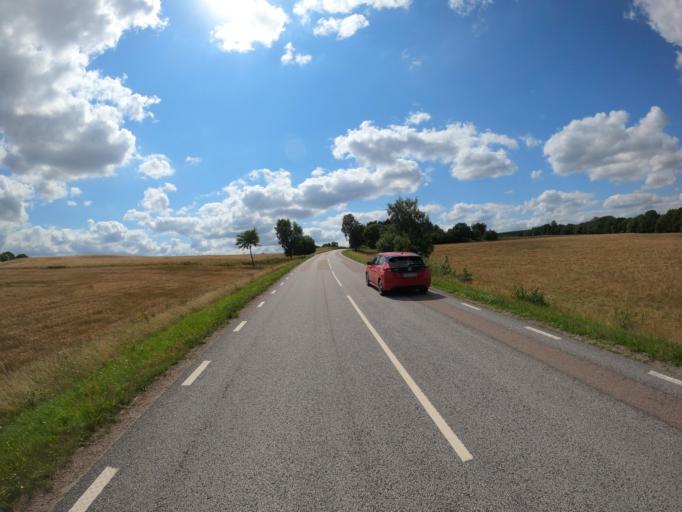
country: SE
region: Skane
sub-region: Lunds Kommun
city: Veberod
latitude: 55.6132
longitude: 13.4922
